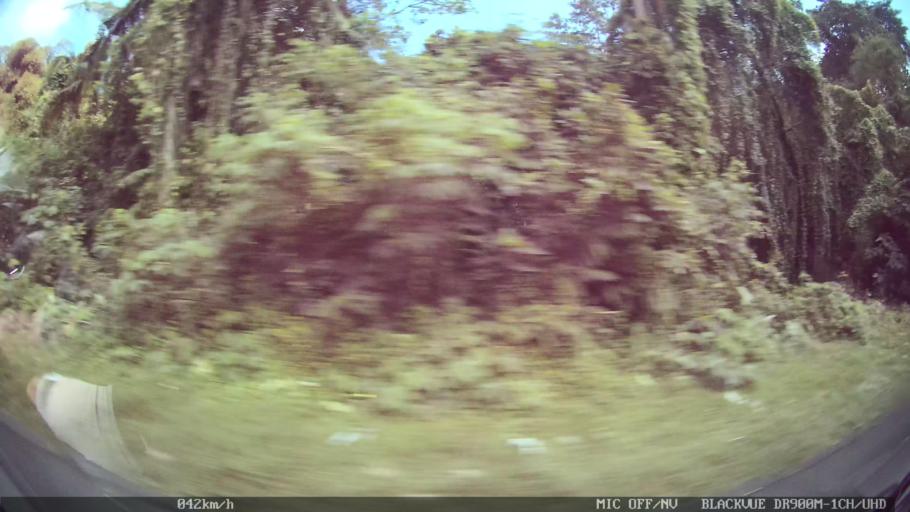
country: ID
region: Bali
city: Banjar Mulung
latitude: -8.5142
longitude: 115.3226
